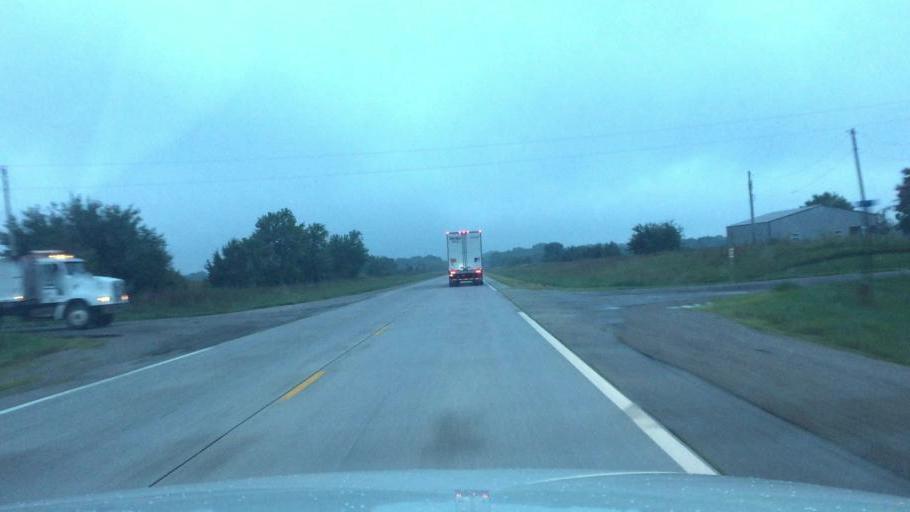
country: US
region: Kansas
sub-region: Neosho County
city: Chanute
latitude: 37.6312
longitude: -95.4797
